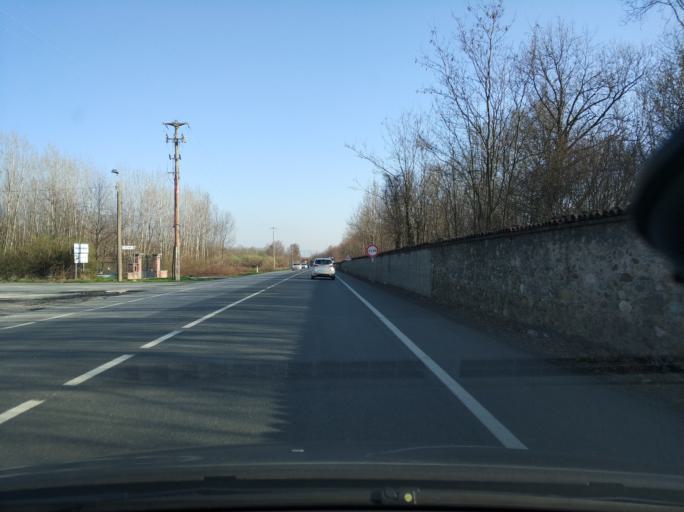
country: IT
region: Piedmont
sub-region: Provincia di Torino
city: Robassomero
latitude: 45.1933
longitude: 7.5633
